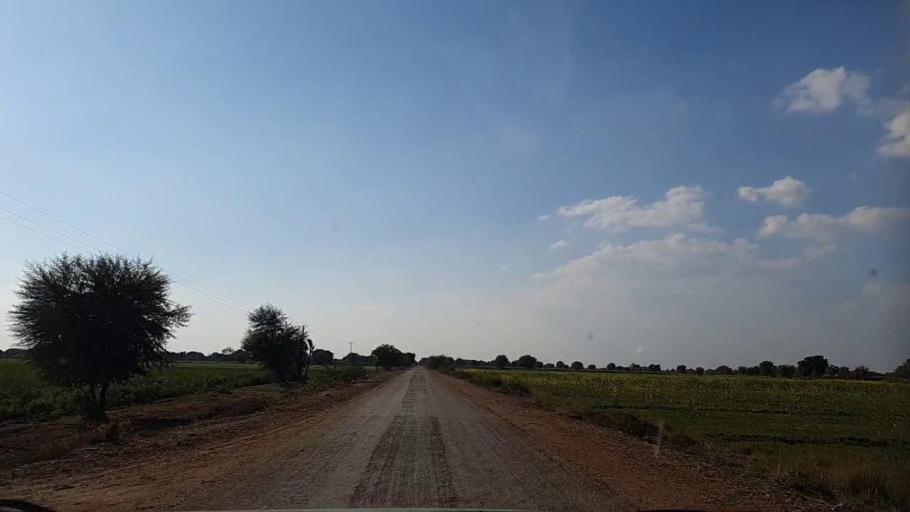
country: PK
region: Sindh
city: Pithoro
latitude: 25.6484
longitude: 69.3106
